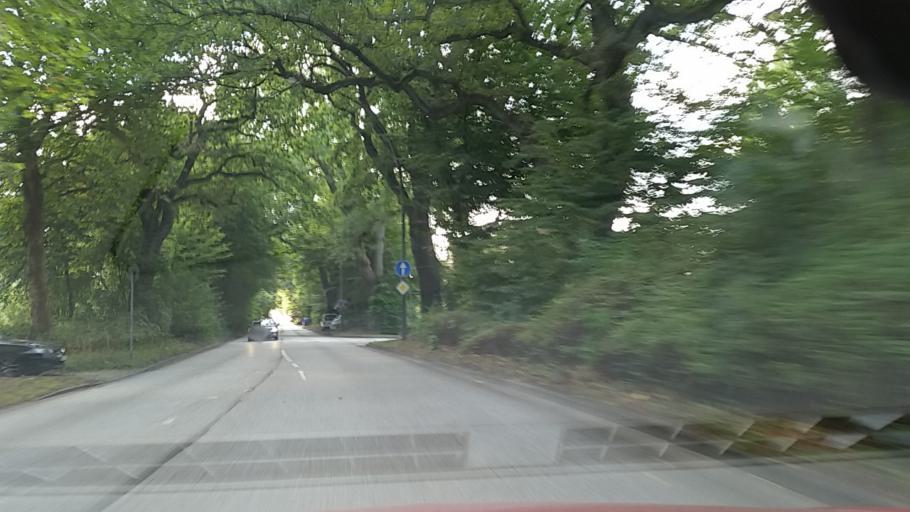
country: DE
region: Hamburg
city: Farmsen-Berne
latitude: 53.6328
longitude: 10.1440
